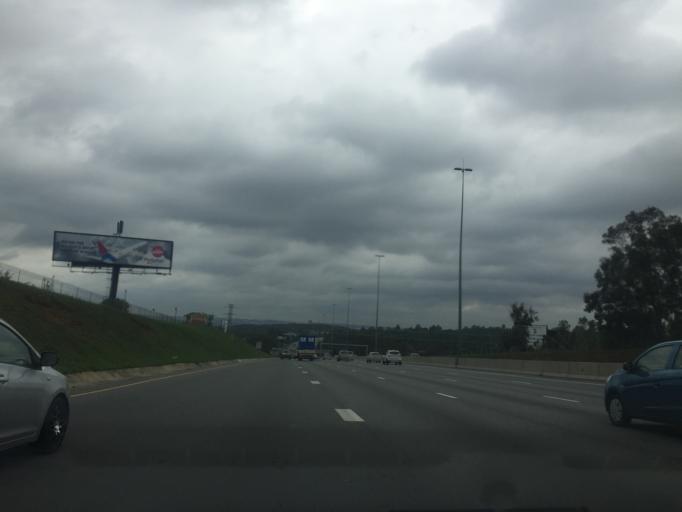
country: ZA
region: Gauteng
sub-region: City of Johannesburg Metropolitan Municipality
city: Diepsloot
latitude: -26.0364
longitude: 28.0202
